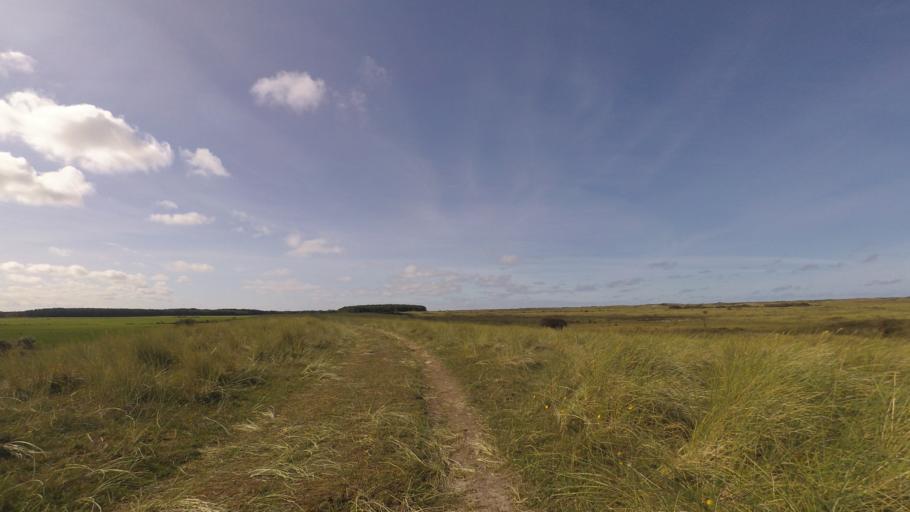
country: NL
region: Friesland
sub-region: Gemeente Ameland
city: Nes
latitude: 53.4500
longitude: 5.7295
